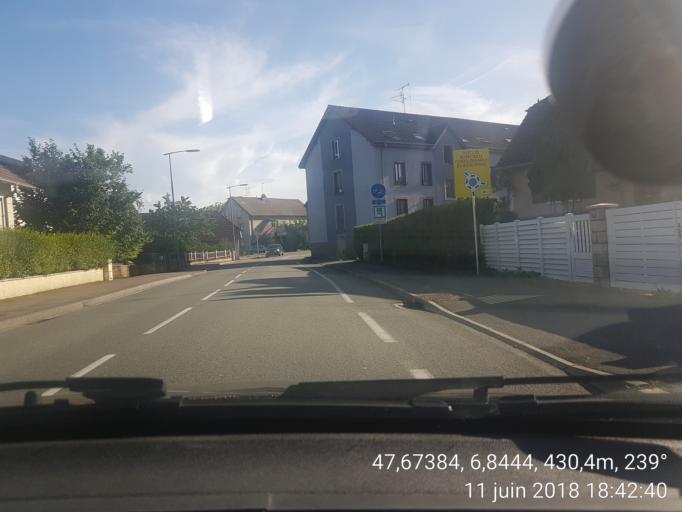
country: FR
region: Franche-Comte
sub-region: Territoire de Belfort
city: Valdoie
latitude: 47.6741
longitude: 6.8442
